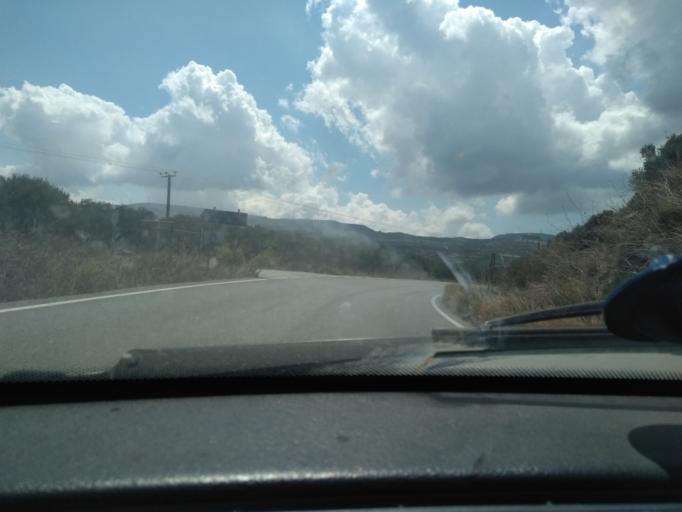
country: GR
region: Crete
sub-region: Nomos Lasithiou
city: Siteia
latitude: 35.1182
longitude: 26.0624
